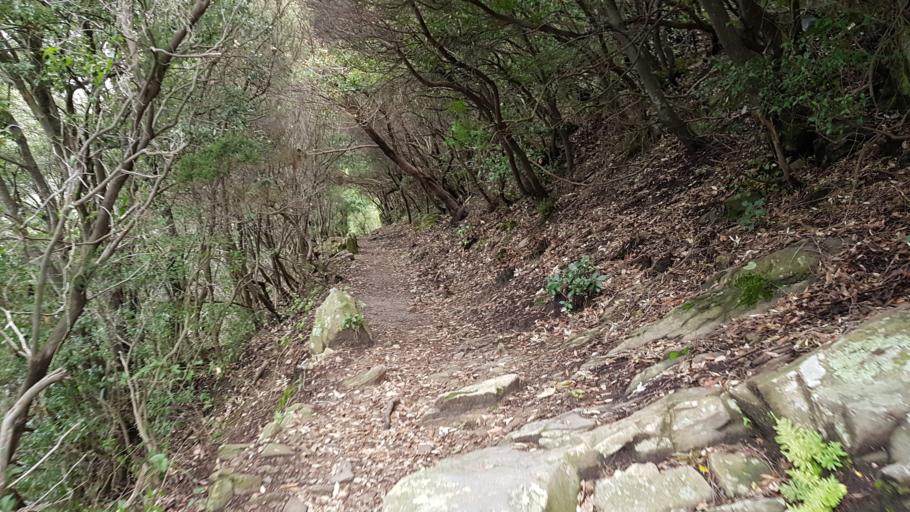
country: IT
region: Liguria
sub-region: Provincia di La Spezia
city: Levanto
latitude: 44.1508
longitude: 9.6201
